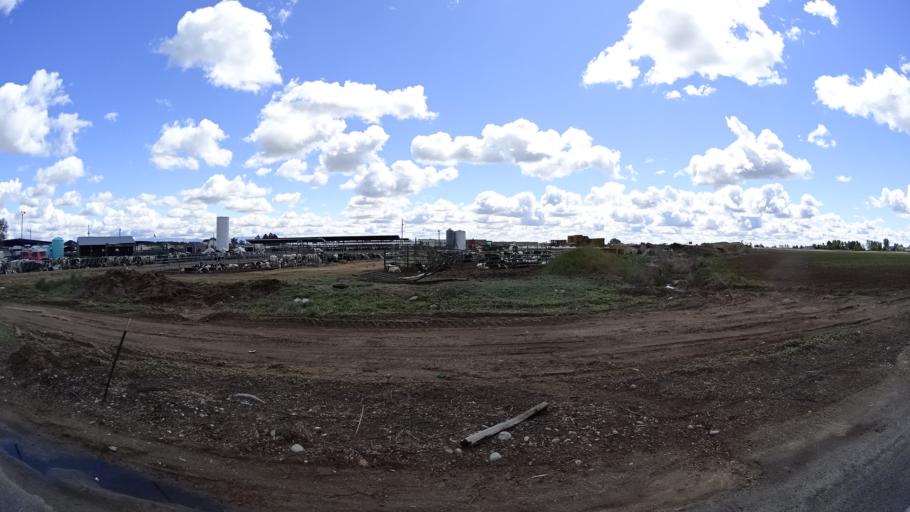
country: US
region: Idaho
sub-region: Ada County
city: Kuna
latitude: 43.5021
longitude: -116.4043
